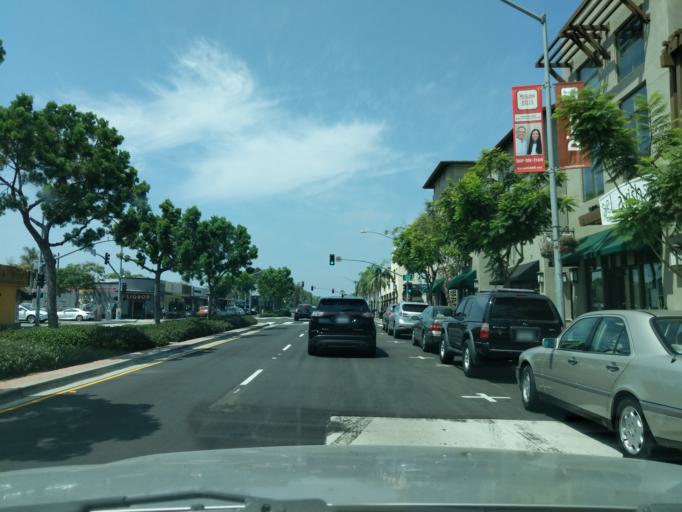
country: US
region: California
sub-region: San Diego County
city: San Diego
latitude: 32.7499
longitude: -117.1699
